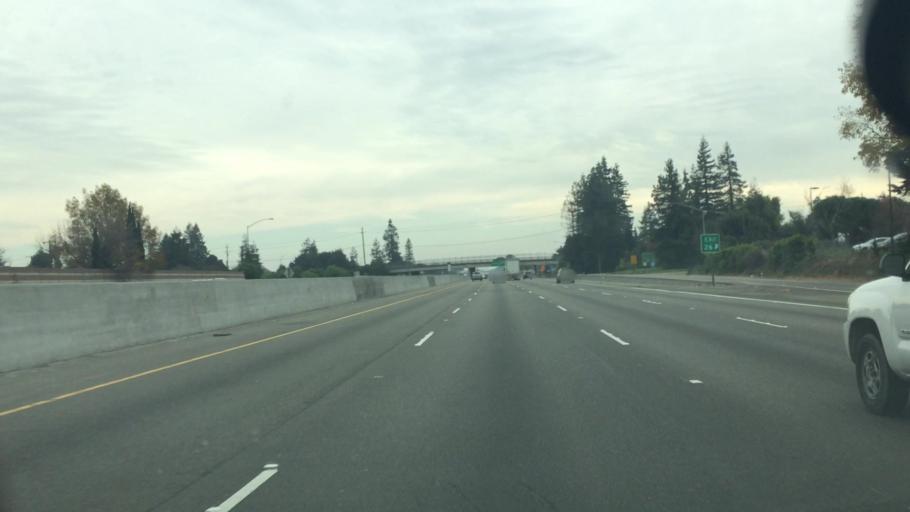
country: US
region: California
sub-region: Alameda County
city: Hayward
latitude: 37.6344
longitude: -122.0865
